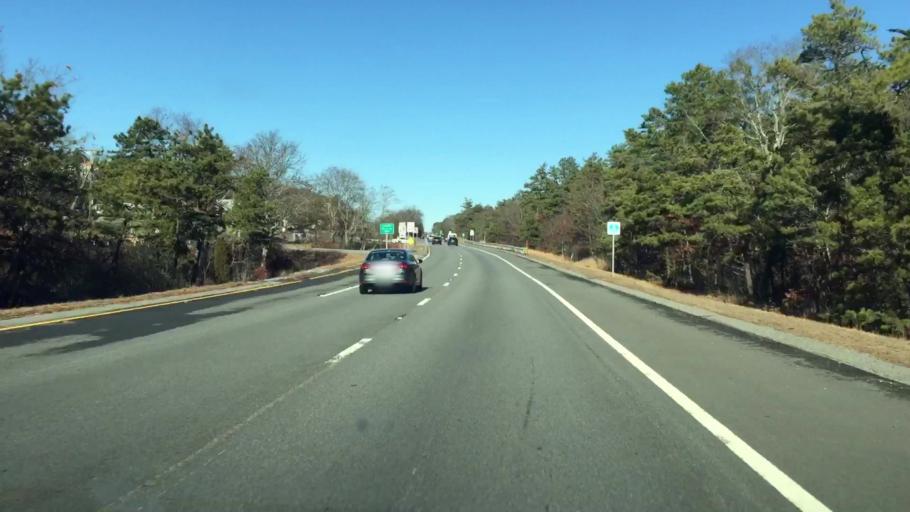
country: US
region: Massachusetts
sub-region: Barnstable County
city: Monument Beach
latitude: 41.7107
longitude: -70.5829
